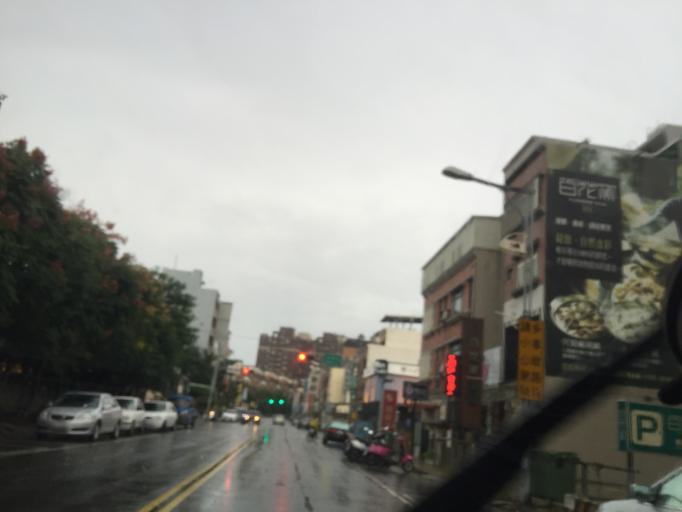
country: TW
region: Taiwan
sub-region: Hsinchu
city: Zhubei
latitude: 24.8317
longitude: 121.0148
